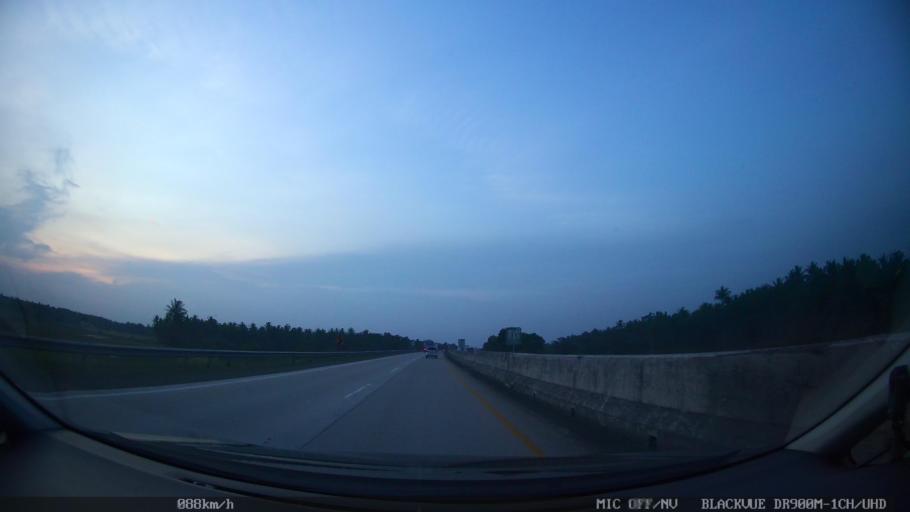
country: ID
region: Lampung
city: Kalianda
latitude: -5.6639
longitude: 105.5935
